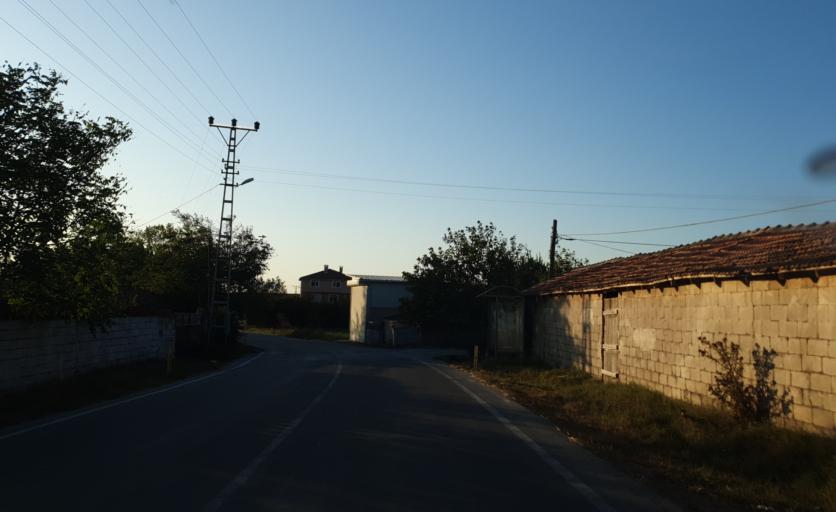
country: TR
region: Tekirdag
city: Beyazkoy
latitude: 41.3372
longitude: 27.7311
